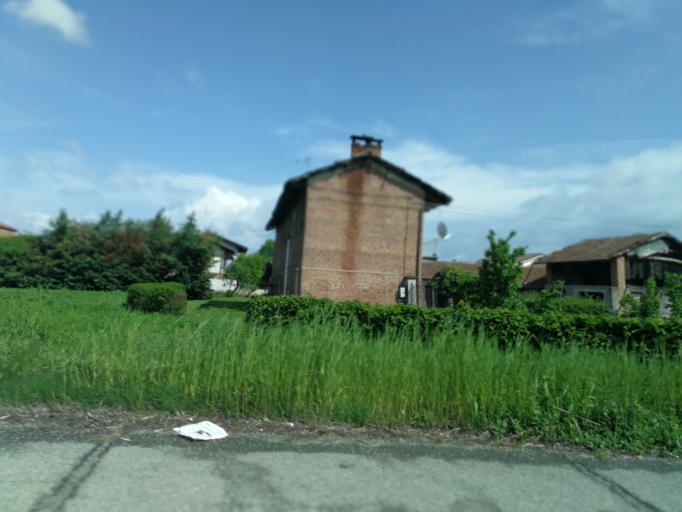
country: IT
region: Piedmont
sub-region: Provincia di Cuneo
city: Moretta
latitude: 44.7660
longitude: 7.5436
